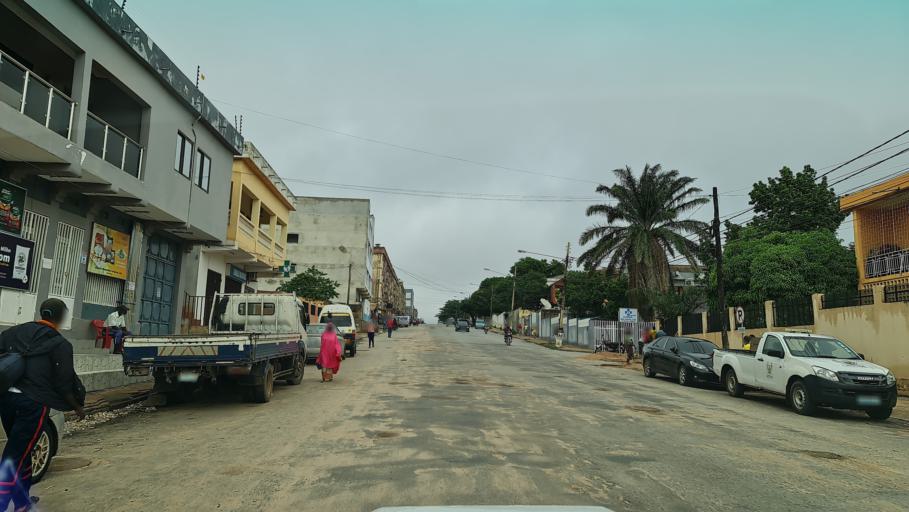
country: MZ
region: Nampula
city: Nampula
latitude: -15.1312
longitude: 39.2685
